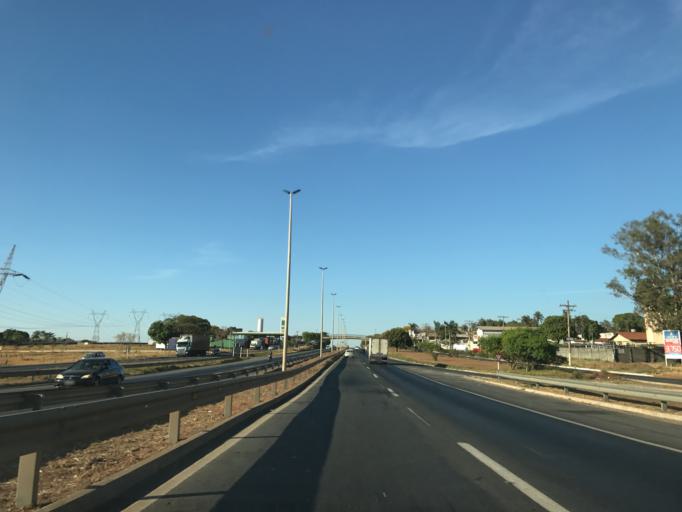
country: BR
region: Goias
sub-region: Aparecida De Goiania
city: Aparecida de Goiania
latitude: -16.8191
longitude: -49.2408
